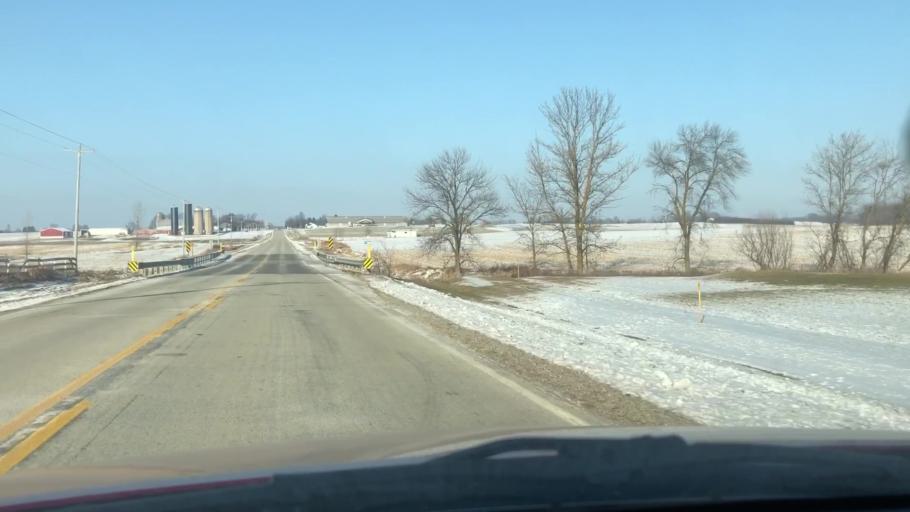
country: US
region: Wisconsin
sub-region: Outagamie County
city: Black Creek
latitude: 44.4029
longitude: -88.3744
